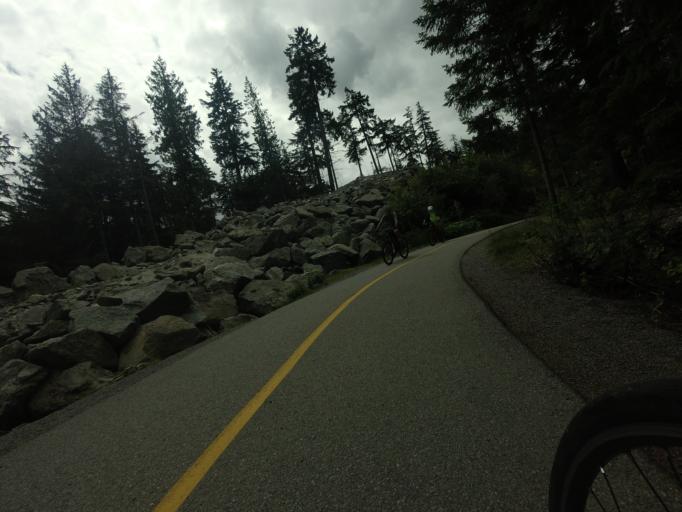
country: CA
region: British Columbia
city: Whistler
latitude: 50.1027
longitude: -122.9902
